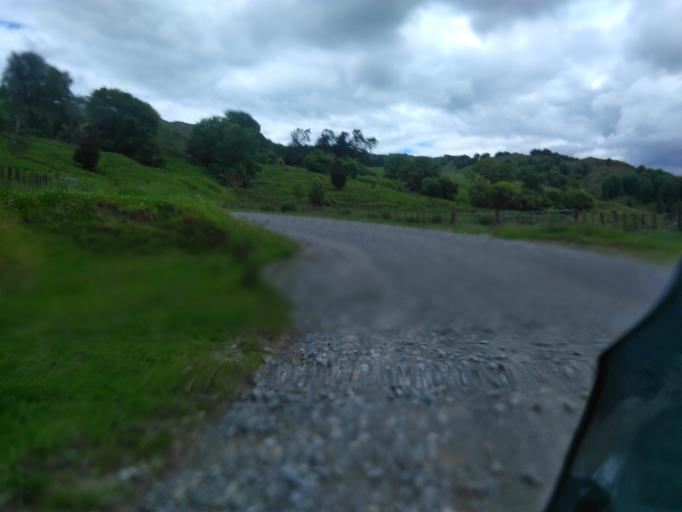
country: NZ
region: Gisborne
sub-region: Gisborne District
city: Gisborne
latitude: -38.0766
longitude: 178.0532
